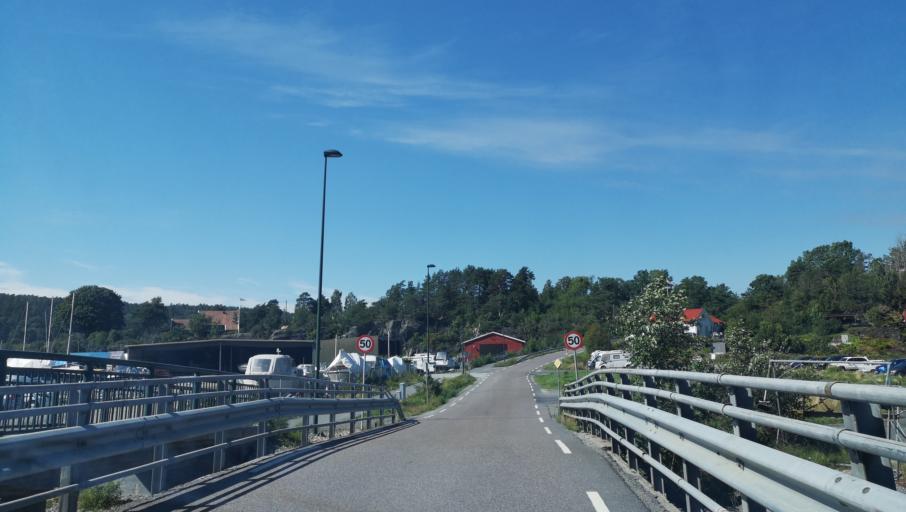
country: NO
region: Ostfold
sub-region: Moss
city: Moss
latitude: 59.5278
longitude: 10.6900
